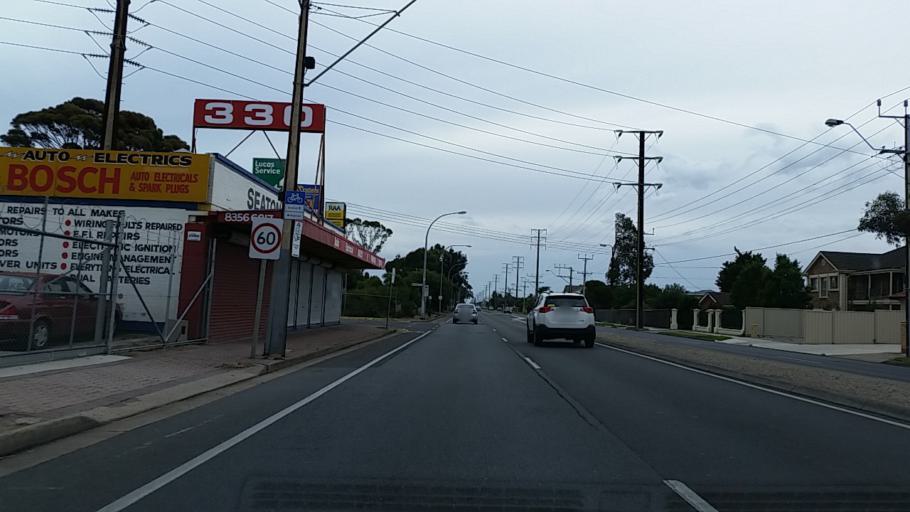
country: AU
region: South Australia
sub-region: Charles Sturt
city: Seaton
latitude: -34.8992
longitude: 138.5142
